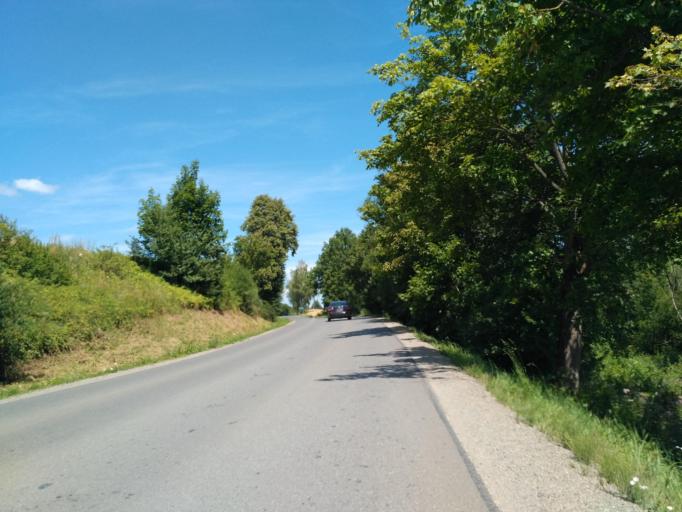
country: PL
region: Subcarpathian Voivodeship
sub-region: Powiat sanocki
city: Nowosielce-Gniewosz
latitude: 49.5333
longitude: 22.1102
